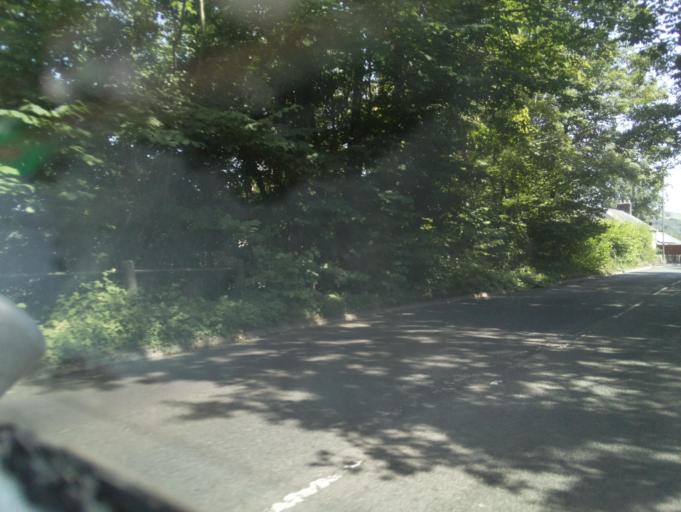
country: GB
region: Wales
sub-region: Caerphilly County Borough
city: Maesycwmmer
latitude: 51.6280
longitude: -3.2342
